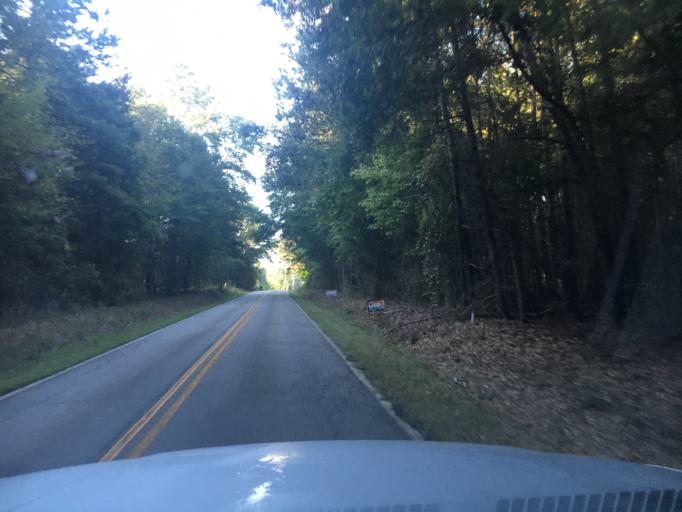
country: US
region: South Carolina
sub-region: Spartanburg County
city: Woodruff
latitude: 34.7578
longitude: -81.9608
